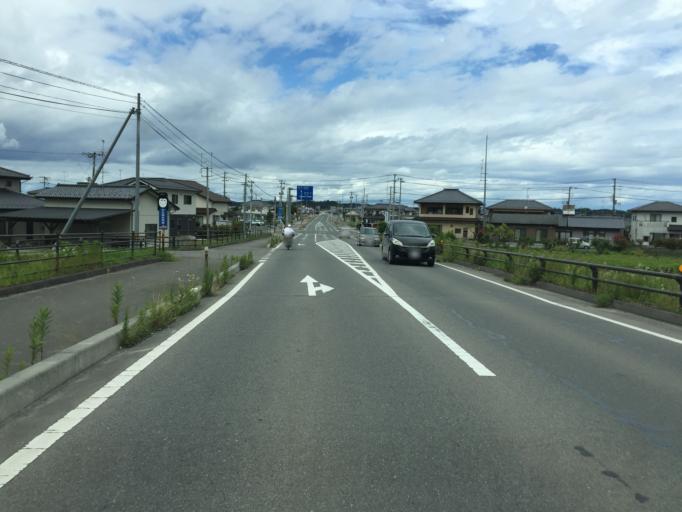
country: JP
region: Fukushima
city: Namie
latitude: 37.6940
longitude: 140.9691
